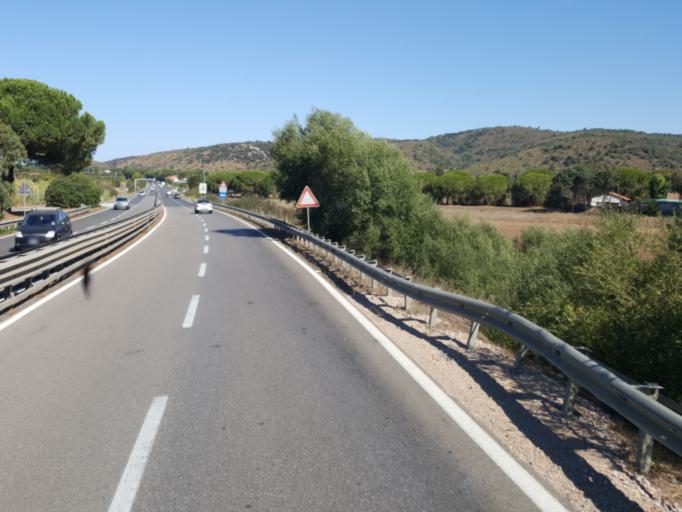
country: IT
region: Tuscany
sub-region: Provincia di Grosseto
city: Orbetello Scalo
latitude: 42.4303
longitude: 11.2853
